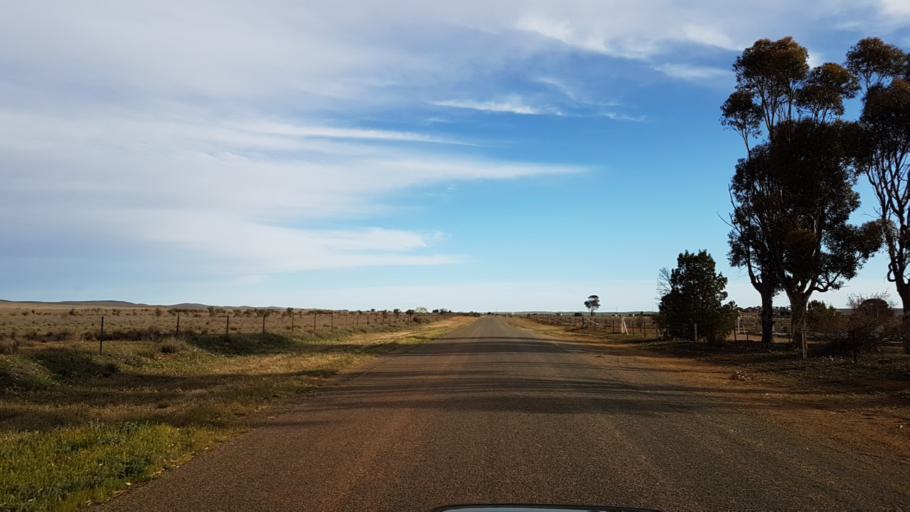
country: AU
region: South Australia
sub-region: Peterborough
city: Peterborough
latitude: -32.9837
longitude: 138.8510
